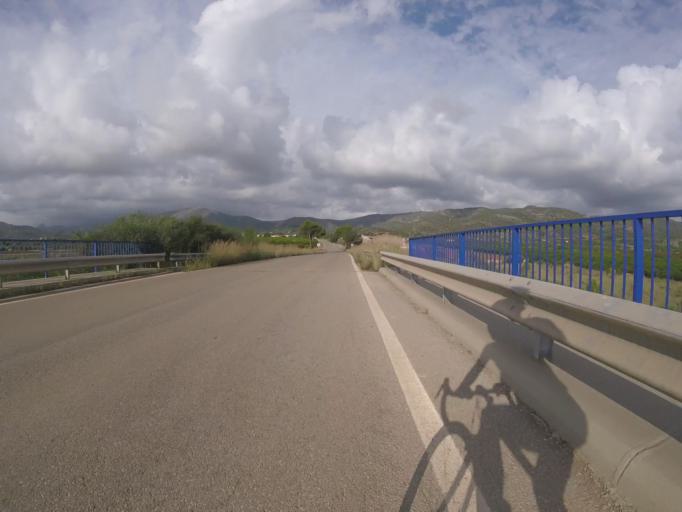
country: ES
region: Valencia
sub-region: Provincia de Castello
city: Orpesa/Oropesa del Mar
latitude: 40.1391
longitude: 0.1421
